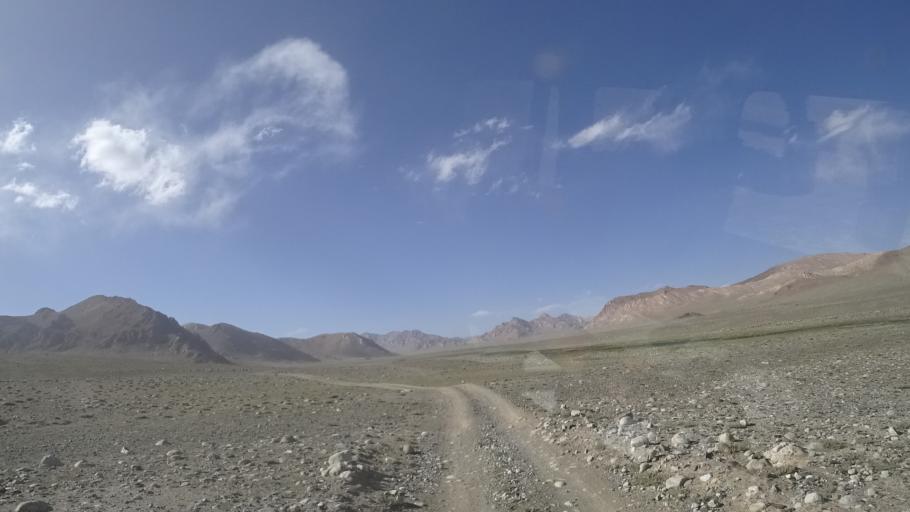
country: TJ
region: Gorno-Badakhshan
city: Murghob
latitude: 37.5805
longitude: 74.1573
